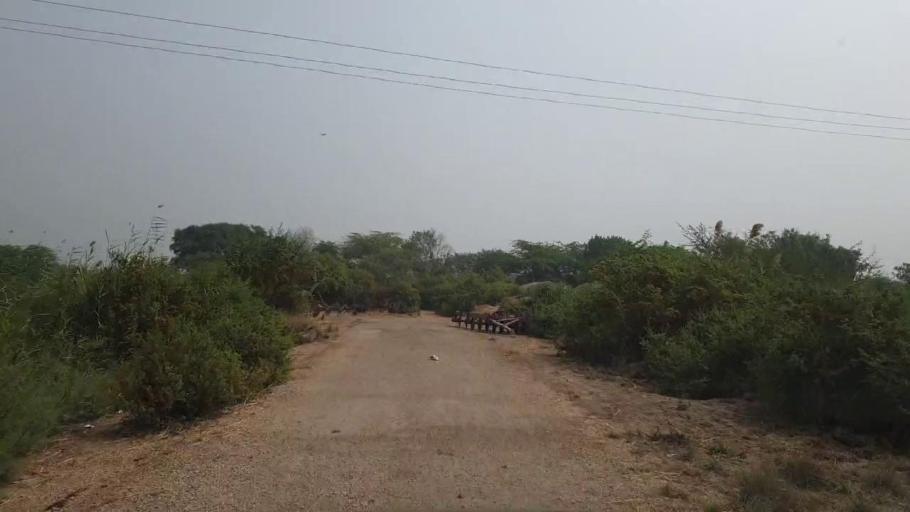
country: PK
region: Sindh
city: Kario
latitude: 24.6570
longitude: 68.6598
